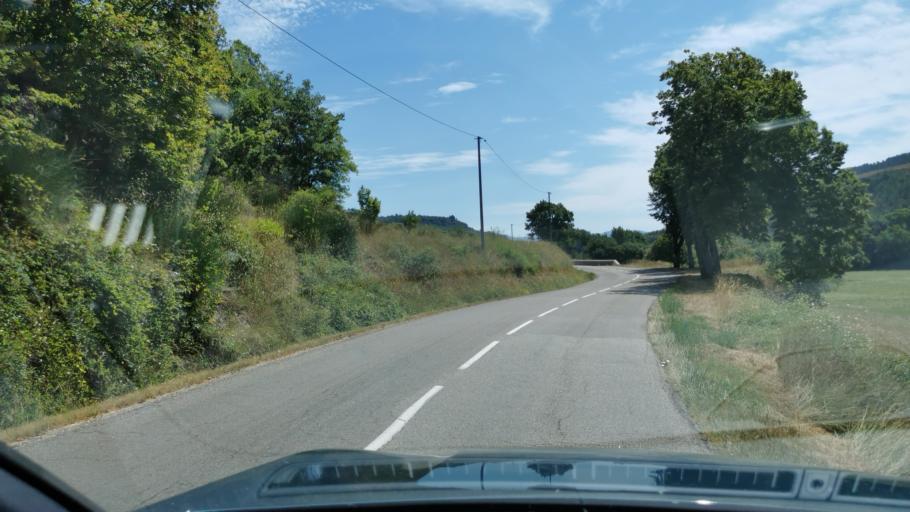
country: FR
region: Rhone-Alpes
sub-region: Departement de la Drome
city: Buis-les-Baronnies
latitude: 44.3011
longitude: 5.3681
